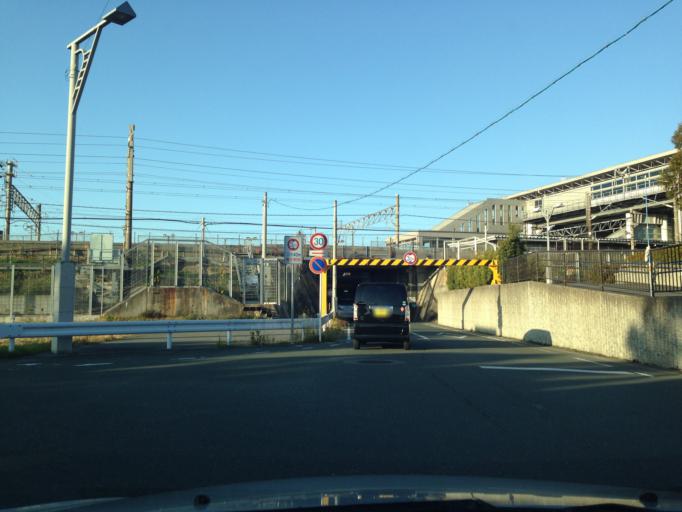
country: JP
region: Shizuoka
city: Fukuroi
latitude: 34.7515
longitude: 137.9611
